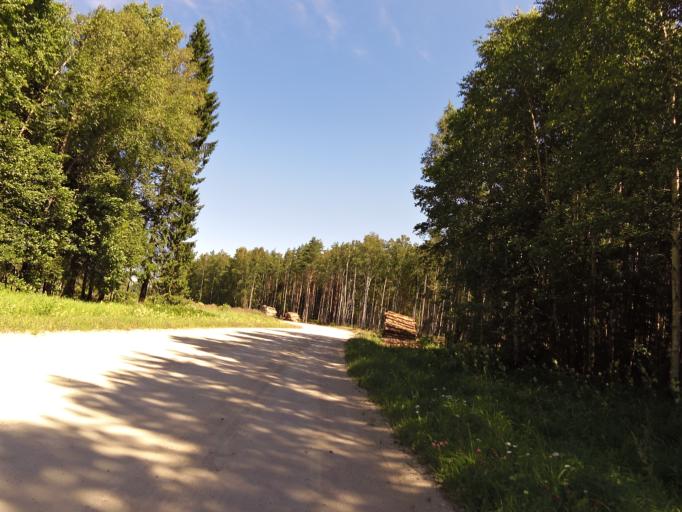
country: EE
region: Hiiumaa
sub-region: Kaerdla linn
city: Kardla
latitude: 58.9236
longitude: 22.3668
